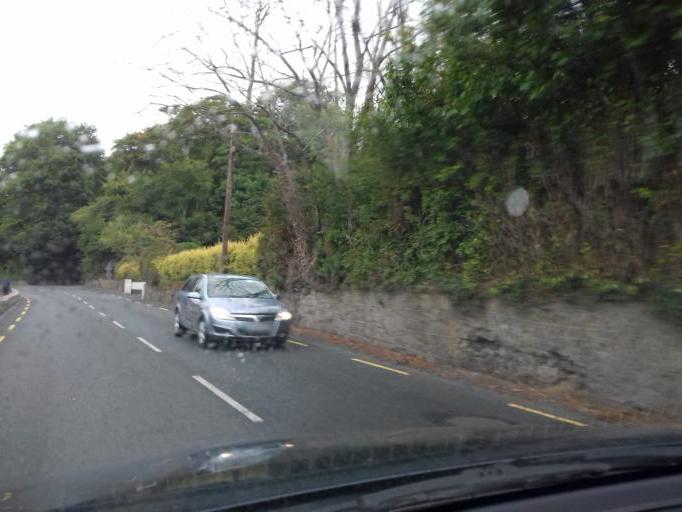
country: IE
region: Leinster
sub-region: County Carlow
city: Bagenalstown
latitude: 52.7082
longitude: -6.9538
